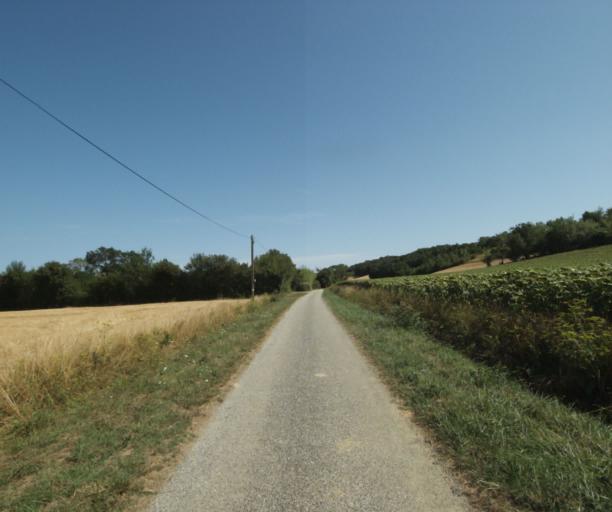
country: FR
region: Midi-Pyrenees
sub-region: Departement de la Haute-Garonne
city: Saint-Felix-Lauragais
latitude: 43.4462
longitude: 1.8409
